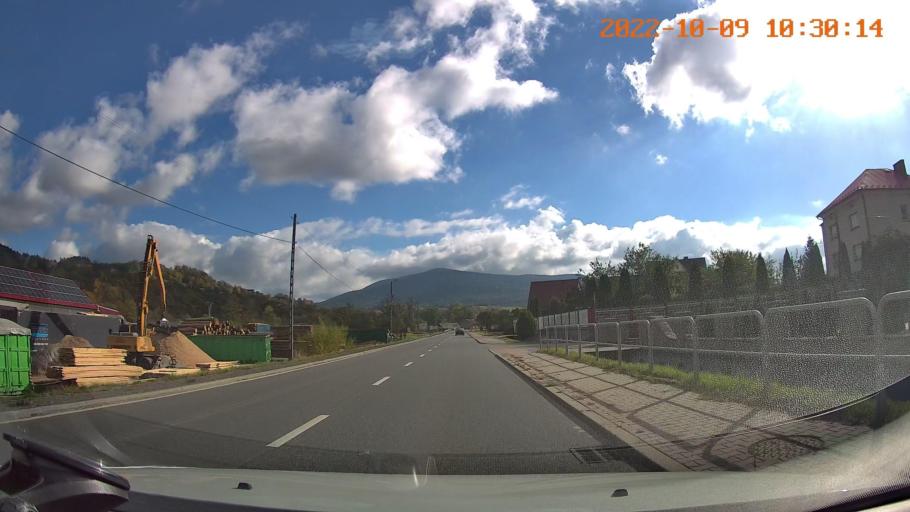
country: PL
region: Lesser Poland Voivodeship
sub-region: Powiat myslenicki
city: Lubien
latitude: 49.7100
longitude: 20.0129
